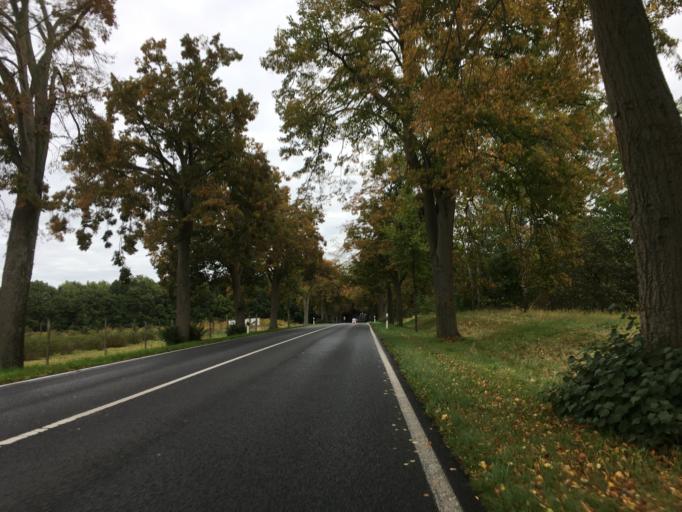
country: DE
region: Brandenburg
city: Werftpfuhl
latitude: 52.6859
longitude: 13.8496
